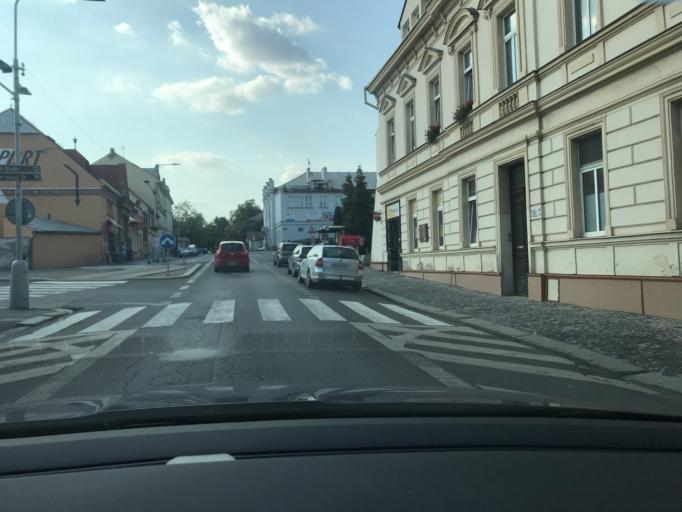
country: CZ
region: Central Bohemia
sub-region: Okres Kladno
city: Slany
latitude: 50.2327
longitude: 14.0812
